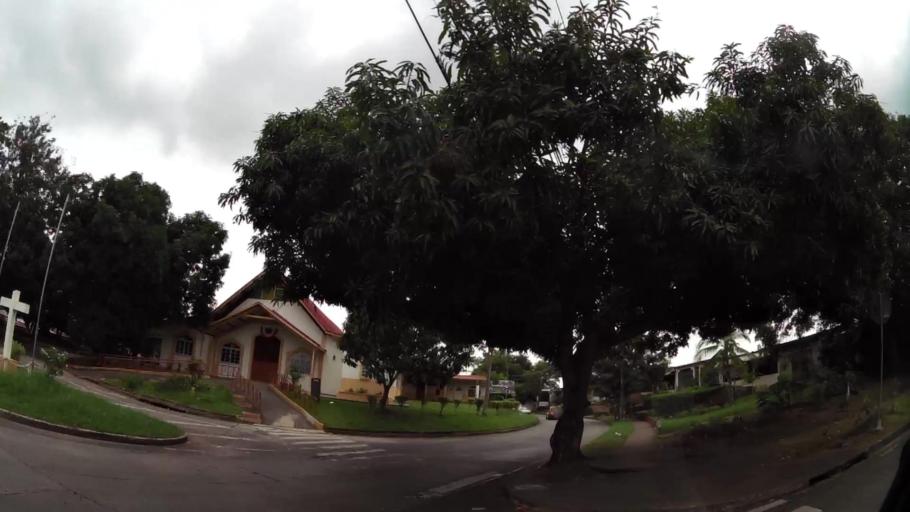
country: PA
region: Panama
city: Tocumen
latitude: 9.0558
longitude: -79.4120
